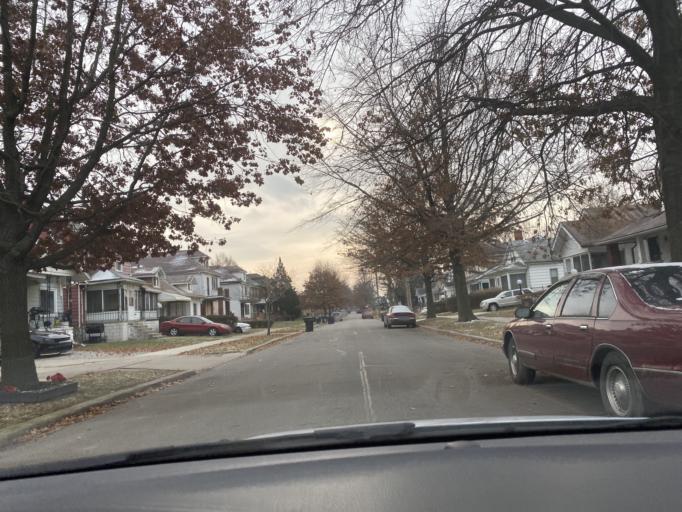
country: US
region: Michigan
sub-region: Wayne County
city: Highland Park
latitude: 42.3721
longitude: -83.1258
